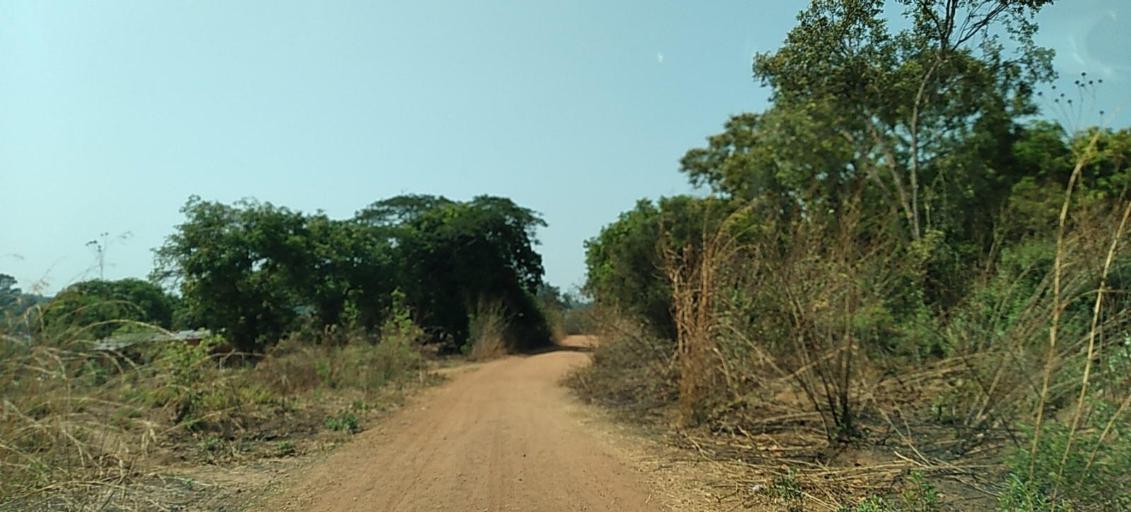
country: ZM
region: Copperbelt
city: Luanshya
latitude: -13.3466
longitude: 28.3935
